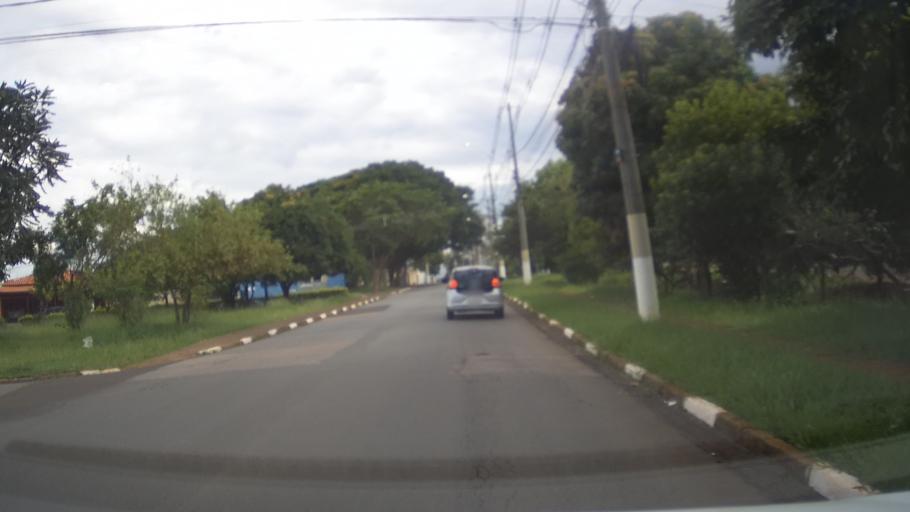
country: BR
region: Sao Paulo
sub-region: Campinas
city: Campinas
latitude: -22.8912
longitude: -47.1236
